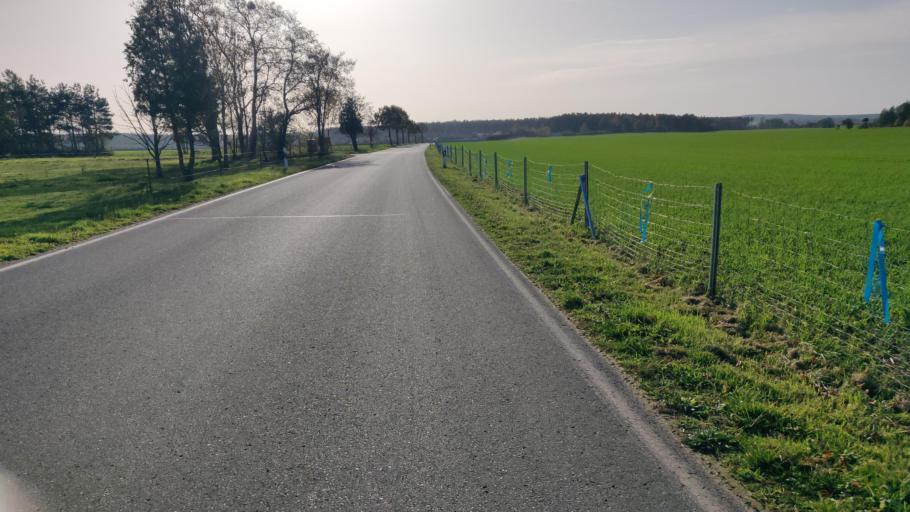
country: DE
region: Brandenburg
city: Kroppen
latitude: 51.3554
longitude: 13.8249
